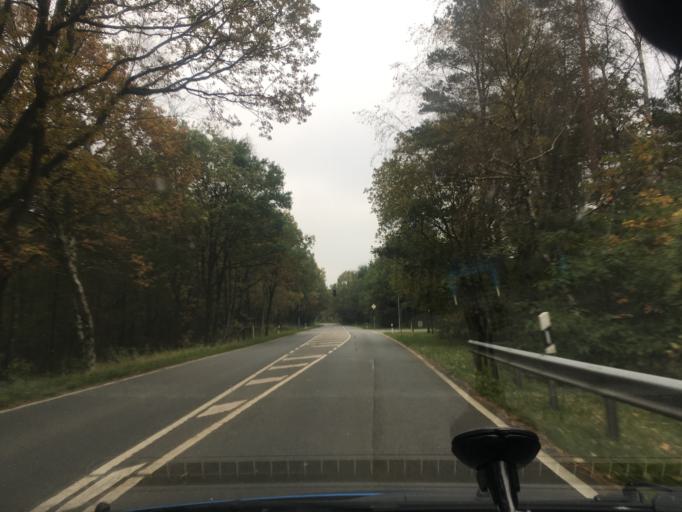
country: DE
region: Lower Saxony
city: Bispingen
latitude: 53.0654
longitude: 9.9949
